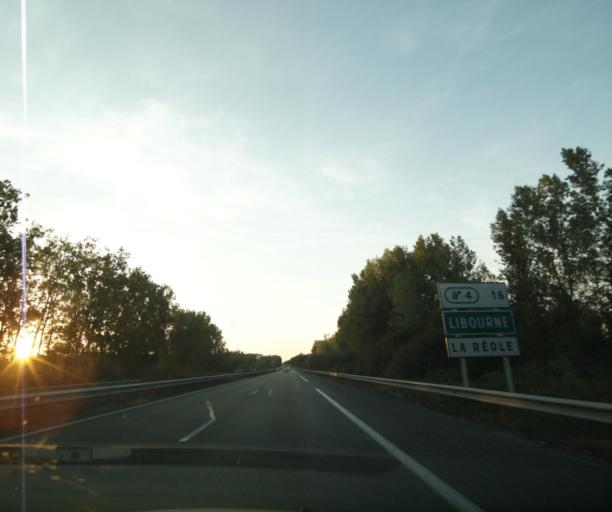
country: FR
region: Aquitaine
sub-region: Departement du Lot-et-Garonne
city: Fourques-sur-Garonne
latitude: 44.4346
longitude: 0.1265
